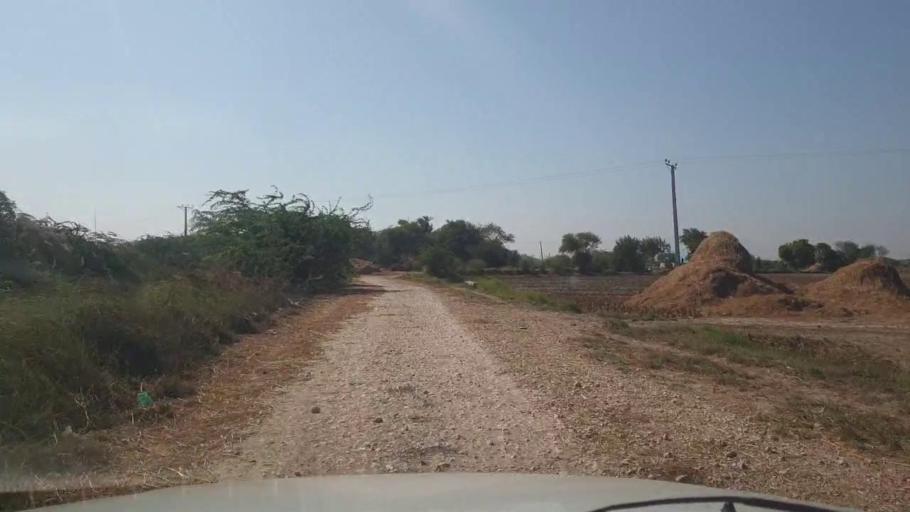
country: PK
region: Sindh
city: Chuhar Jamali
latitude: 24.4273
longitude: 67.7987
